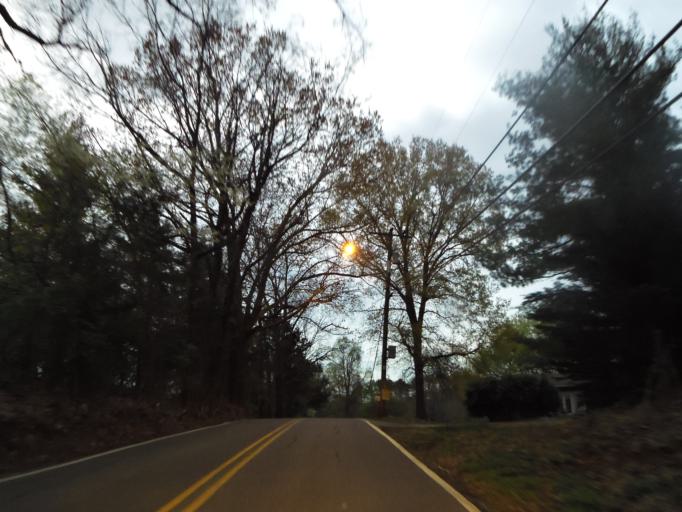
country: US
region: Tennessee
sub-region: Knox County
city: Farragut
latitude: 35.9332
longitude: -84.0587
